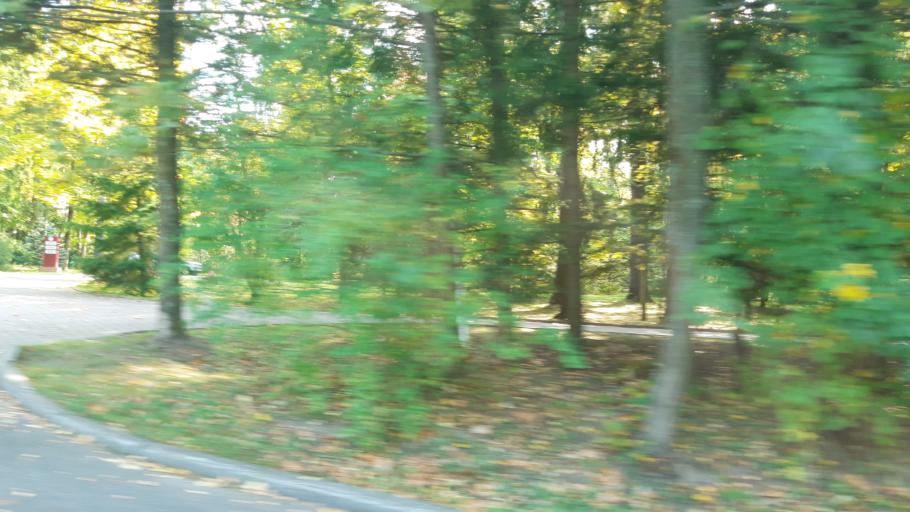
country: RU
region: Moskovskaya
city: Mendeleyevo
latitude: 56.0525
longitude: 37.2216
